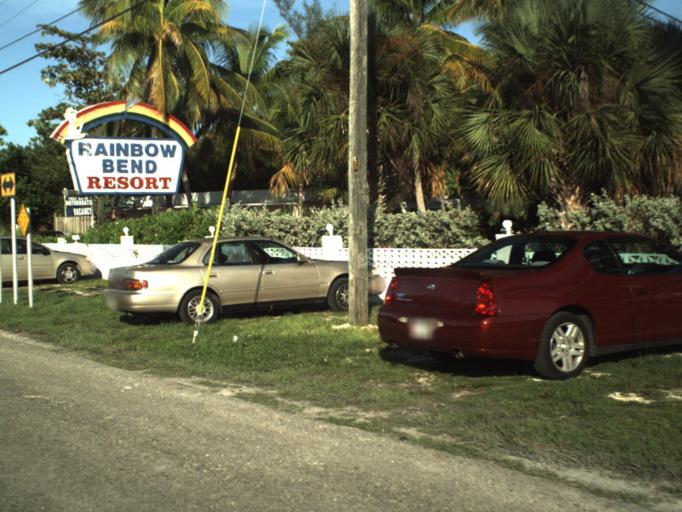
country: US
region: Florida
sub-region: Monroe County
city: Marathon
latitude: 24.7565
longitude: -80.9588
